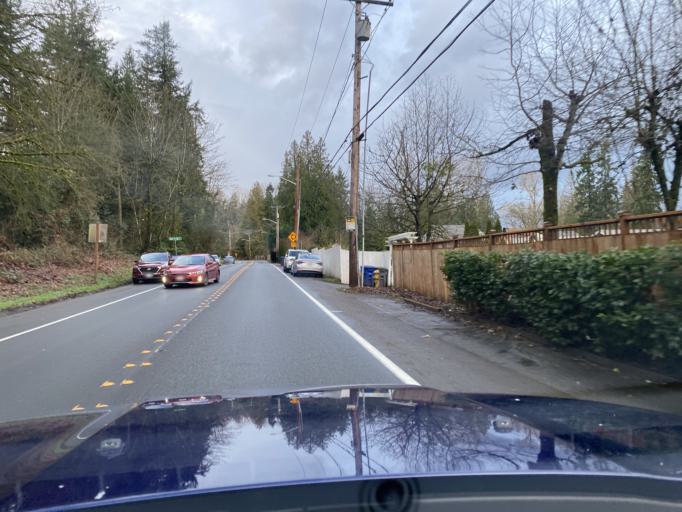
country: US
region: Washington
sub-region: King County
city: West Lake Sammamish
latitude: 47.5717
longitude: -122.1185
